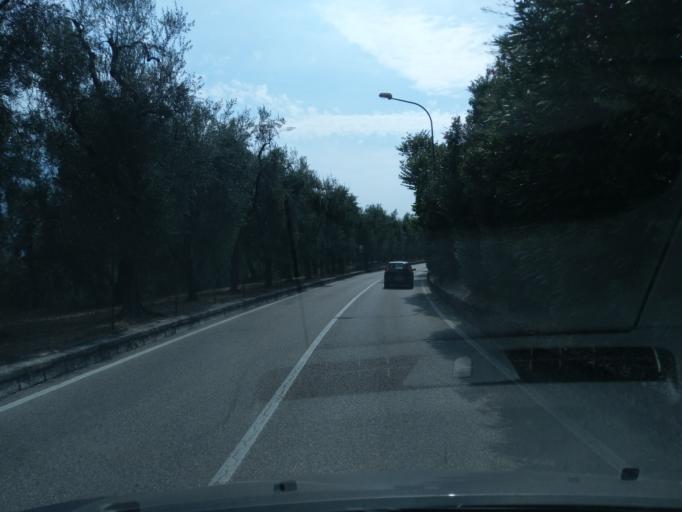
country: IT
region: Lombardy
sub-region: Provincia di Brescia
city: Limone sul Garda
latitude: 45.8044
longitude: 10.7874
